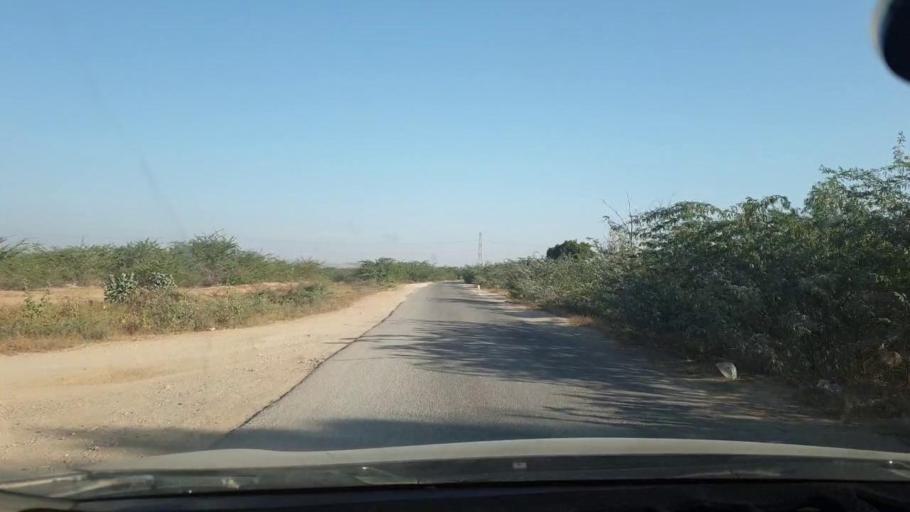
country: PK
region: Sindh
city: Malir Cantonment
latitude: 25.1544
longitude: 67.1909
